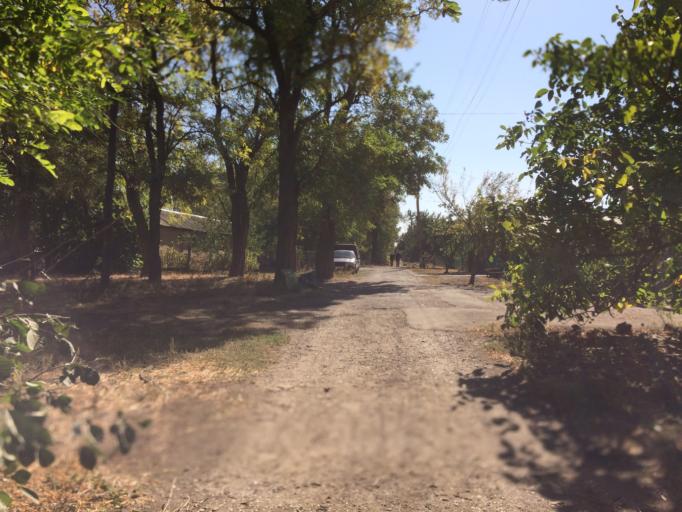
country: RU
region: Rostov
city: Gigant
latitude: 46.5176
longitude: 41.1877
